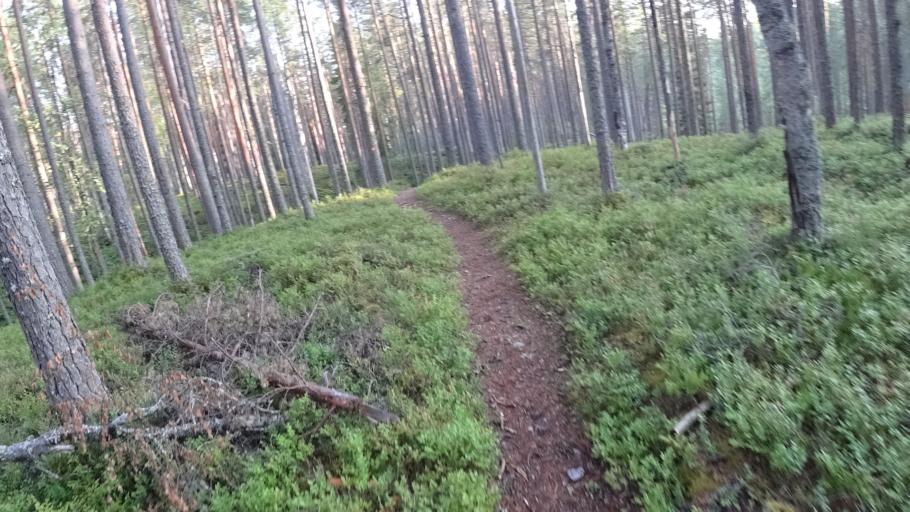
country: FI
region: North Karelia
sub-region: Joensuu
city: Ilomantsi
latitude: 62.5833
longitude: 31.1637
